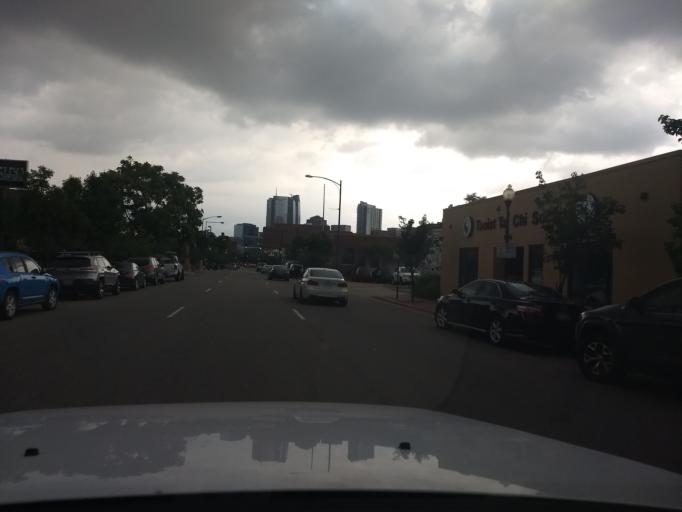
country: US
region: Colorado
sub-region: Denver County
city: Denver
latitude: 39.7341
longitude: -104.9987
